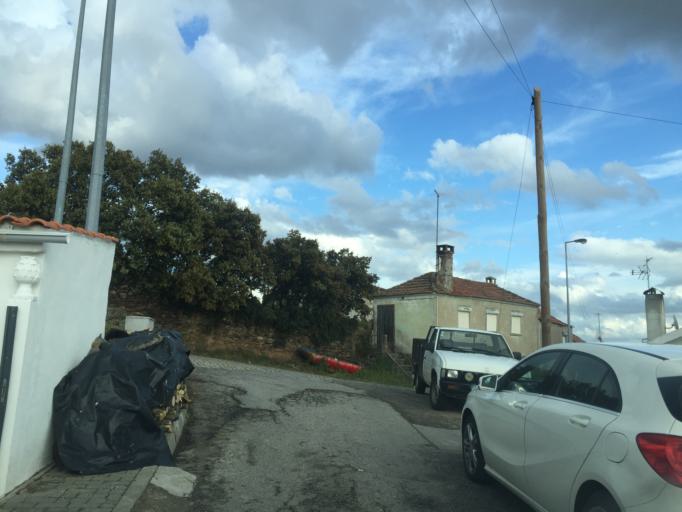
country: PT
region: Braganca
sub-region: Alfandega da Fe
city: Alfandega da Fe
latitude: 41.3401
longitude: -6.9661
